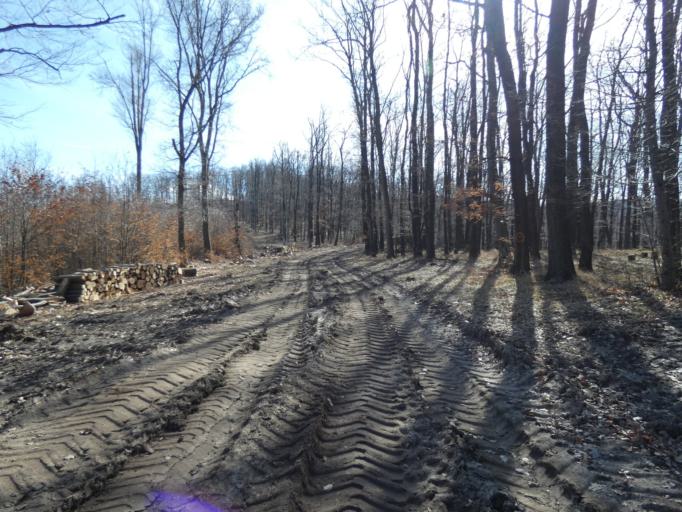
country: SK
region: Nitriansky
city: Sahy
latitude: 47.9820
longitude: 18.9563
